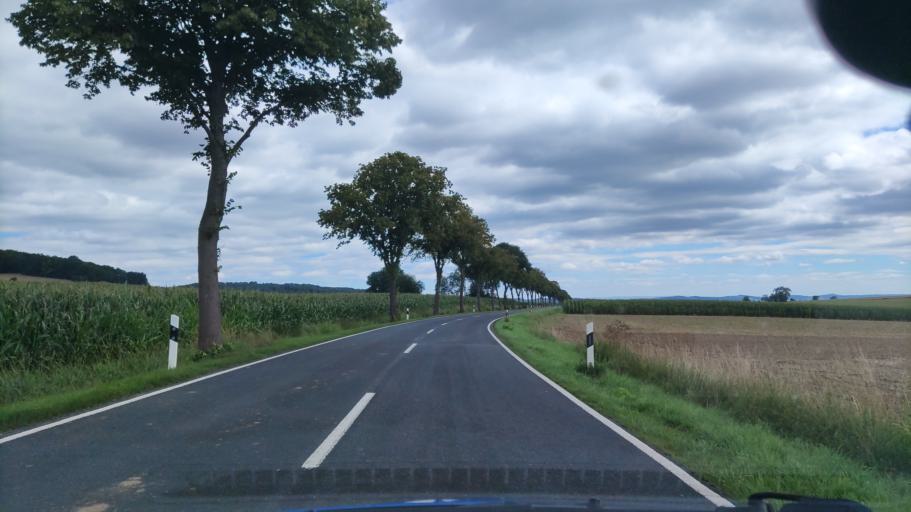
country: DE
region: Lower Saxony
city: Eimen
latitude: 51.8353
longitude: 9.7715
